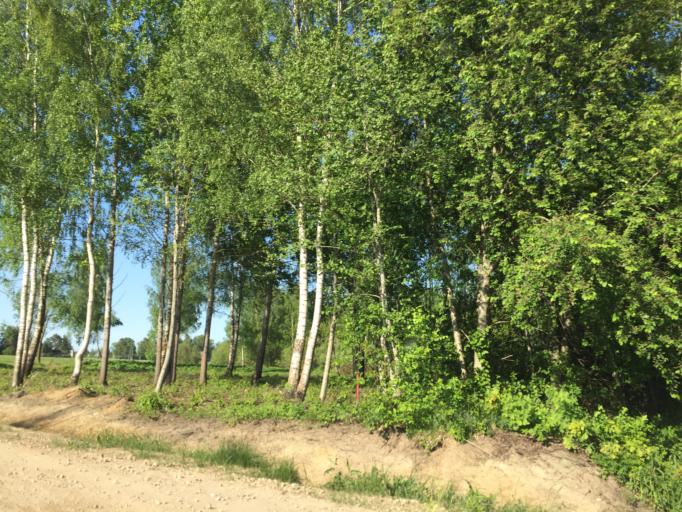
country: LV
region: Kekava
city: Kekava
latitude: 56.8217
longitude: 24.2625
